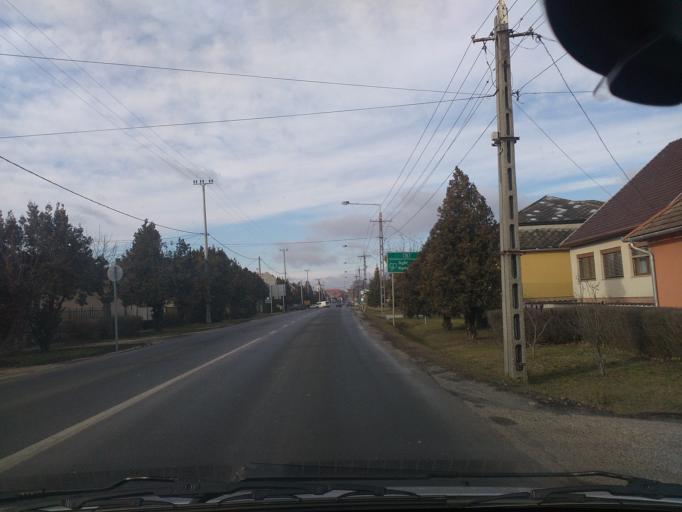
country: HU
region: Komarom-Esztergom
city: Tat
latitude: 47.7406
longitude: 18.6516
